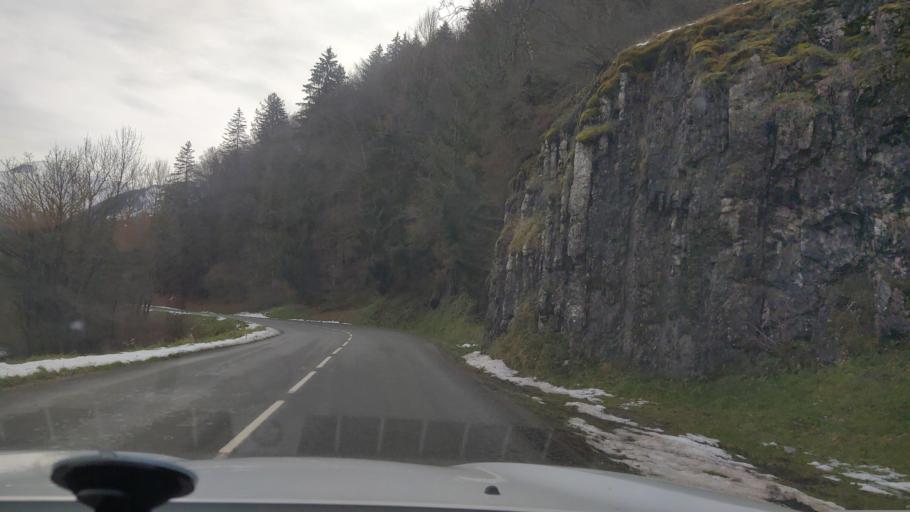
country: FR
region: Rhone-Alpes
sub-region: Departement de la Savoie
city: Gresy-sur-Isere
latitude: 45.6623
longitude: 6.1605
